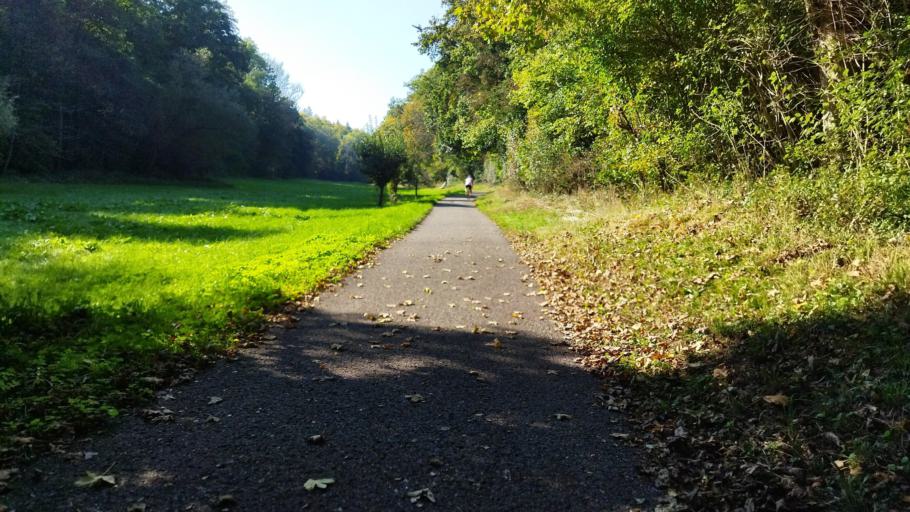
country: DE
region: Baden-Wuerttemberg
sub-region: Regierungsbezirk Stuttgart
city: Besigheim
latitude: 49.0115
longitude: 9.1276
